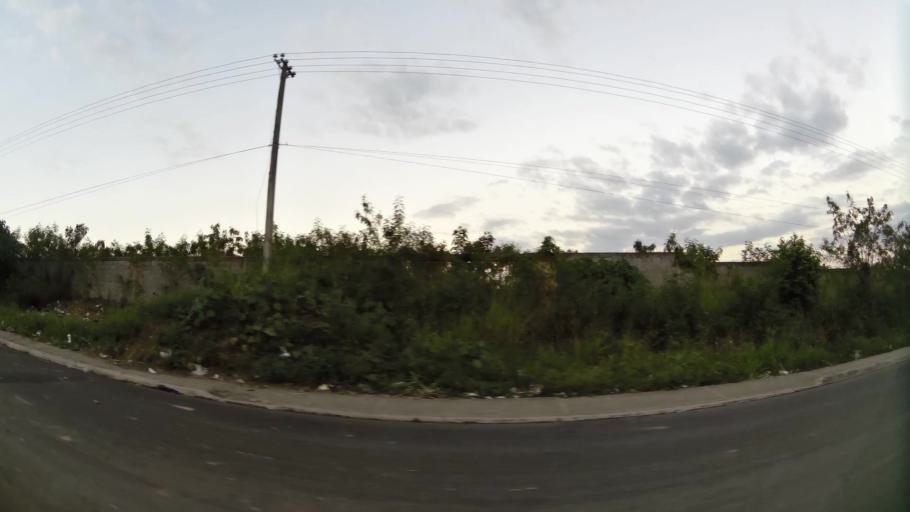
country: DO
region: Nacional
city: La Agustina
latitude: 18.5553
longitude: -69.9482
